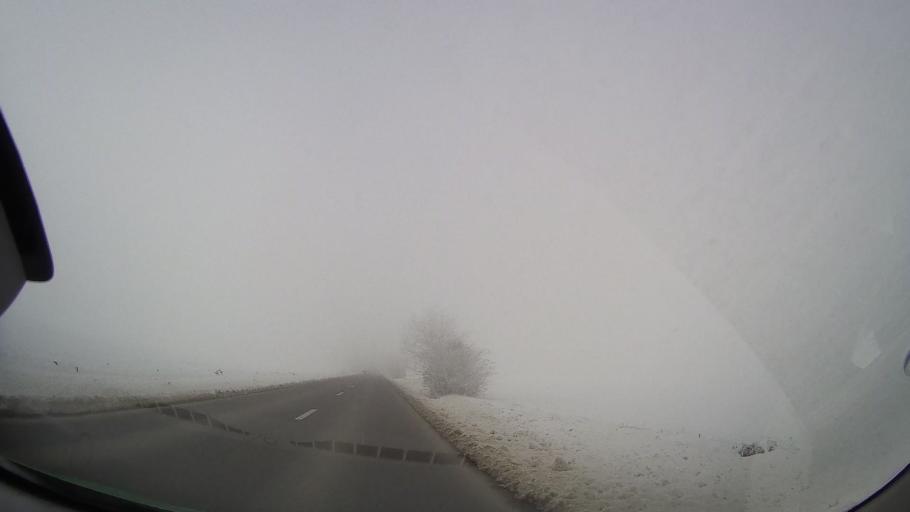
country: RO
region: Iasi
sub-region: Comuna Stolniceni-Prajescu
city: Stolniceni-Prajescu
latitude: 47.1843
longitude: 26.7428
